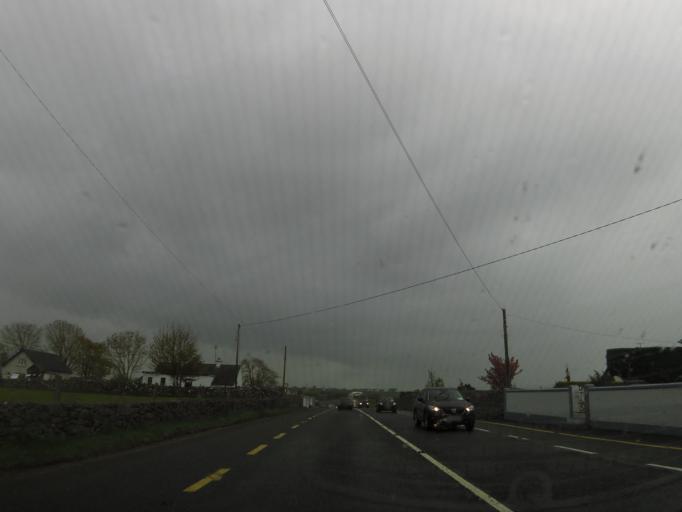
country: IE
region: Connaught
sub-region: County Galway
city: Tuam
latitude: 53.4980
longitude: -8.8889
